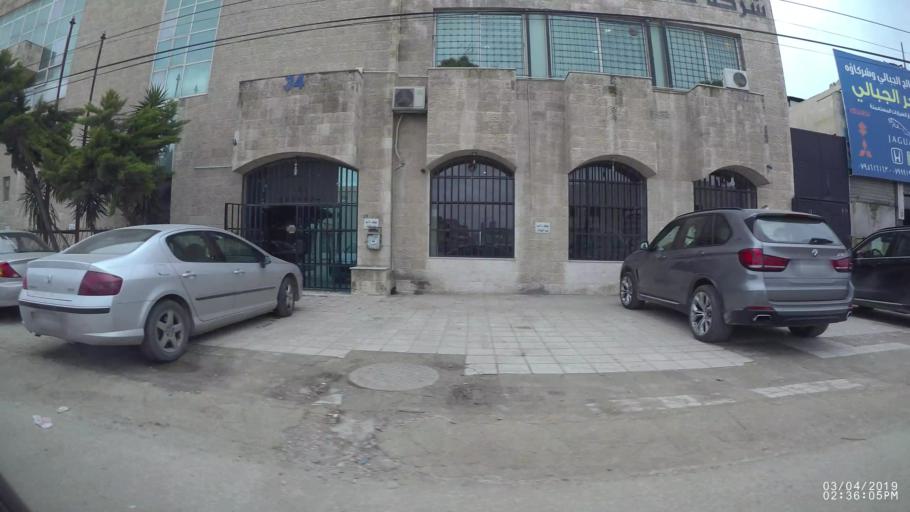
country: JO
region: Amman
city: Wadi as Sir
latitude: 31.9424
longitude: 35.8398
